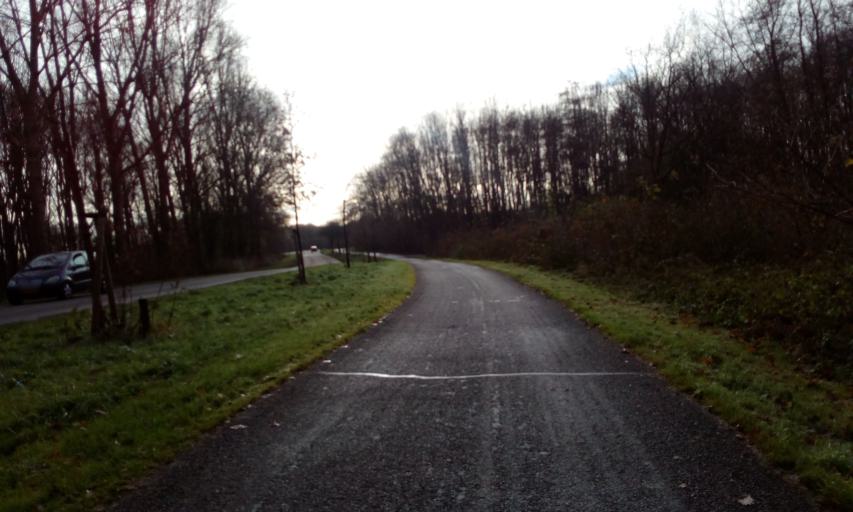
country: NL
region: South Holland
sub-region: Gemeente Lansingerland
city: Bergschenhoek
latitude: 51.9641
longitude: 4.5183
